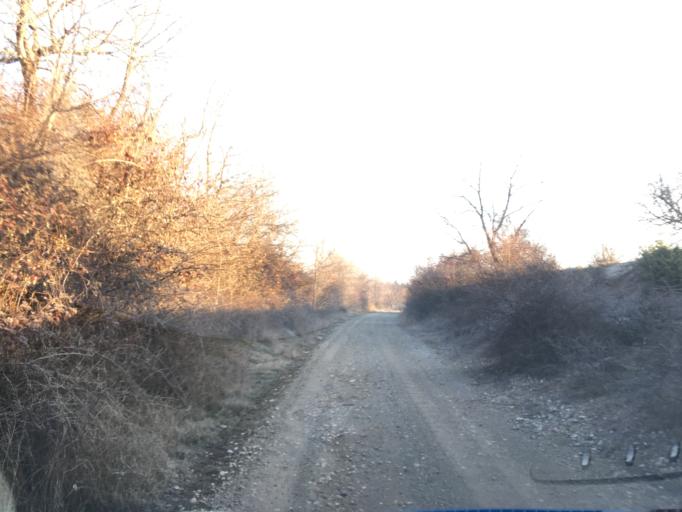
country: GR
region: West Macedonia
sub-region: Nomos Kozanis
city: Kozani
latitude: 40.2798
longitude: 21.7651
